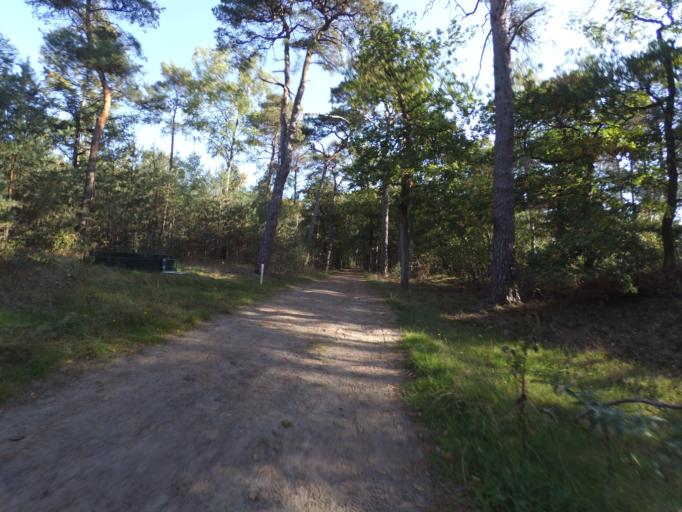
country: NL
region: Utrecht
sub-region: Gemeente De Bilt
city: De Bilt
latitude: 52.1143
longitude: 5.2120
